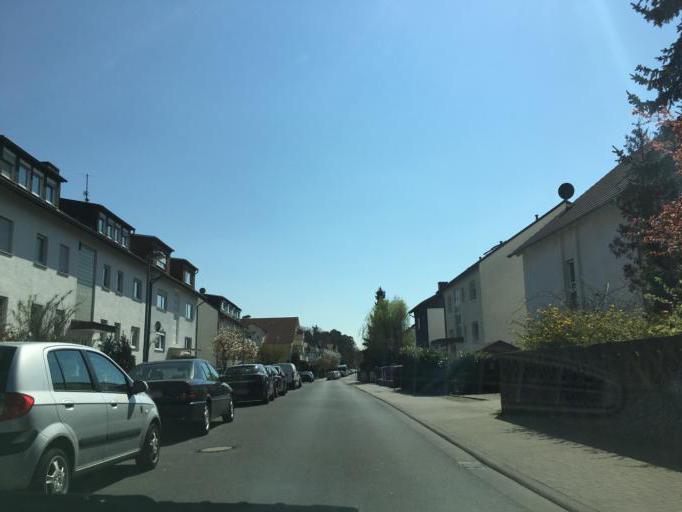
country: DE
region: Hesse
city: Obertshausen
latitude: 50.0703
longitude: 8.8571
